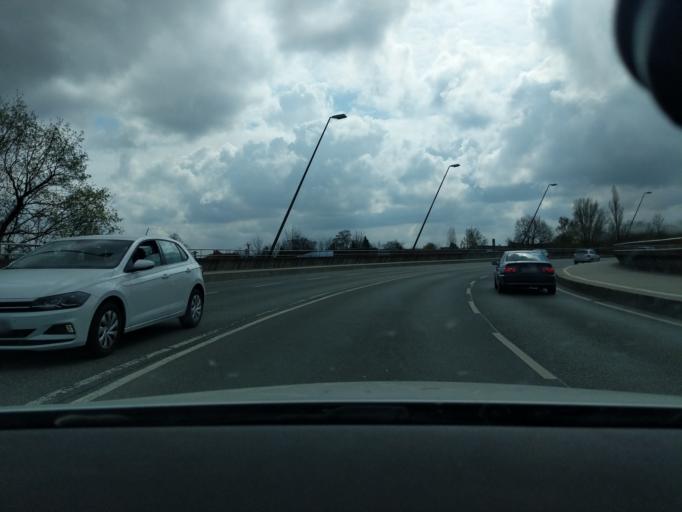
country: DE
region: Lower Saxony
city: Stade
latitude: 53.5969
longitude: 9.4783
